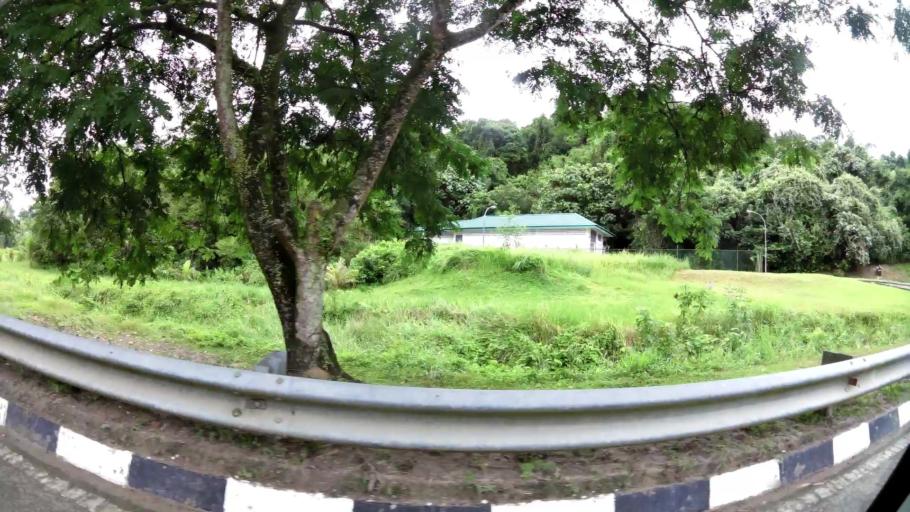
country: BN
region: Brunei and Muara
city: Bandar Seri Begawan
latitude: 4.8876
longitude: 114.9330
